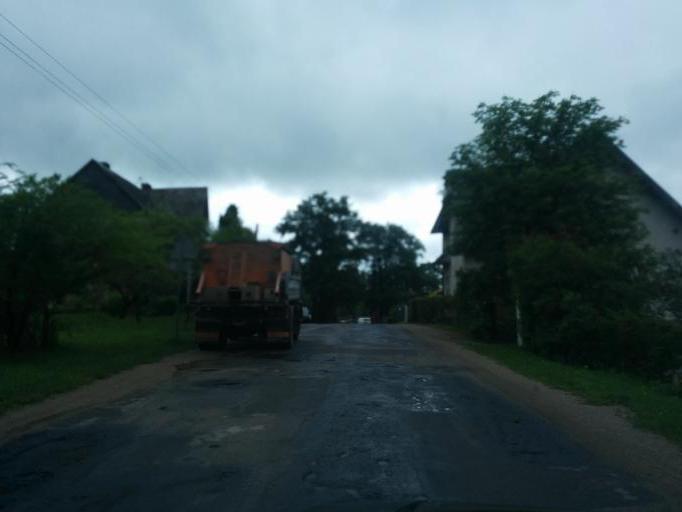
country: LV
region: Smiltene
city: Smiltene
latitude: 57.4264
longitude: 25.8944
